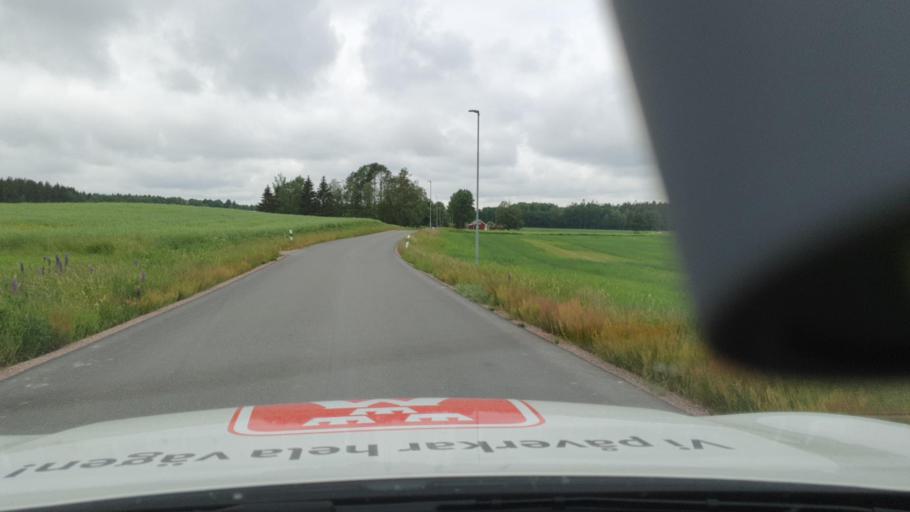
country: SE
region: Vaestra Goetaland
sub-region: Tibro Kommun
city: Tibro
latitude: 58.4073
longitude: 14.1768
